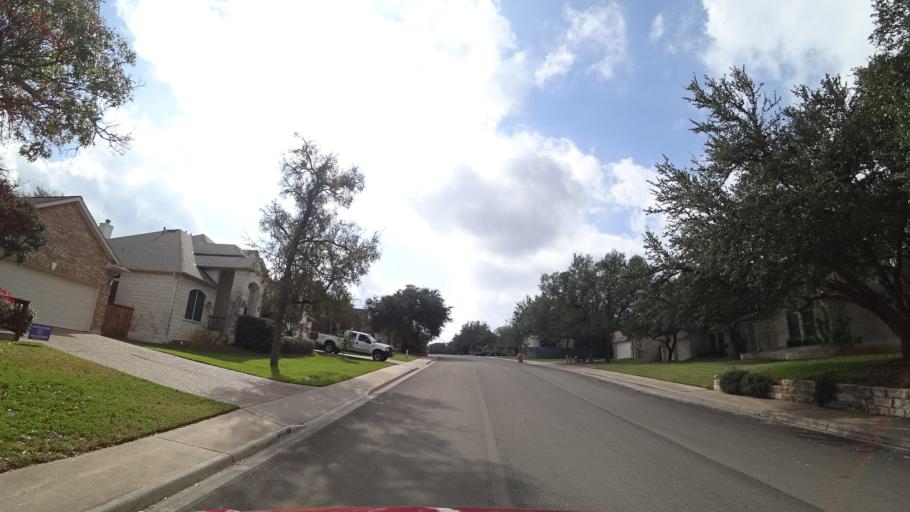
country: US
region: Texas
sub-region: Williamson County
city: Anderson Mill
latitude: 30.4216
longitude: -97.8564
